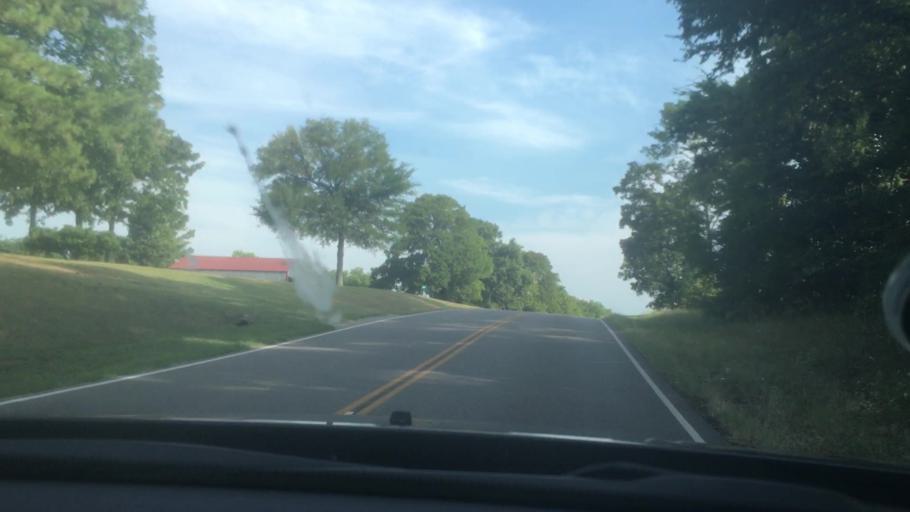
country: US
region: Oklahoma
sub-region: Pontotoc County
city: Ada
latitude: 34.7357
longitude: -96.6713
